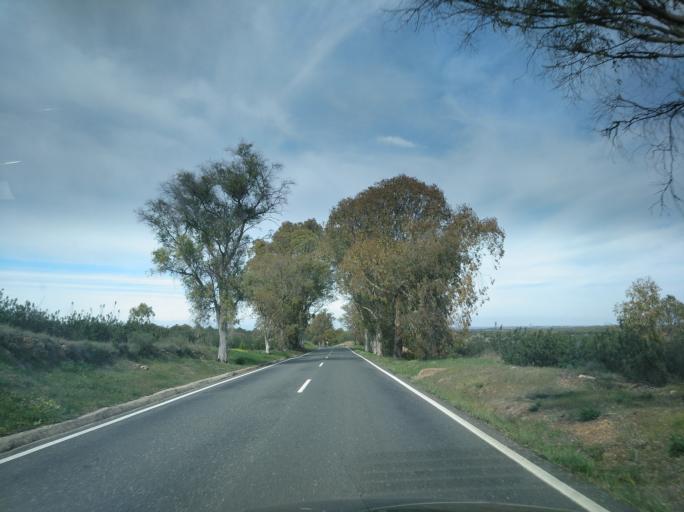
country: PT
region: Beja
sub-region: Mertola
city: Mertola
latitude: 37.7108
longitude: -7.7540
